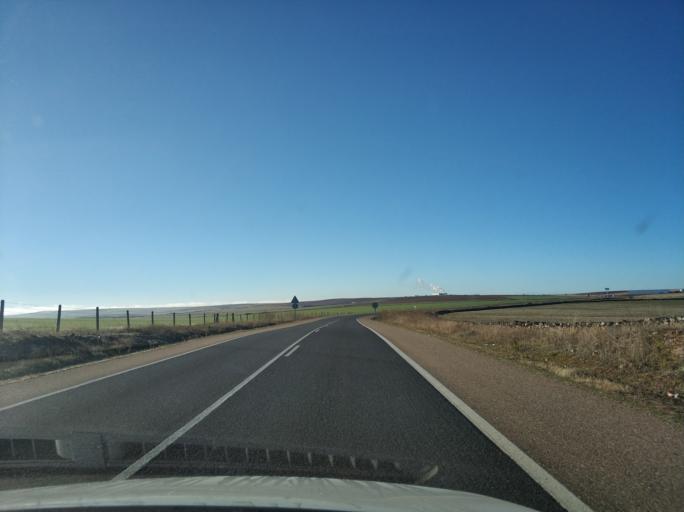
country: ES
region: Castille and Leon
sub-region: Provincia de Salamanca
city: Aldeatejada
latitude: 40.9041
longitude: -5.7151
